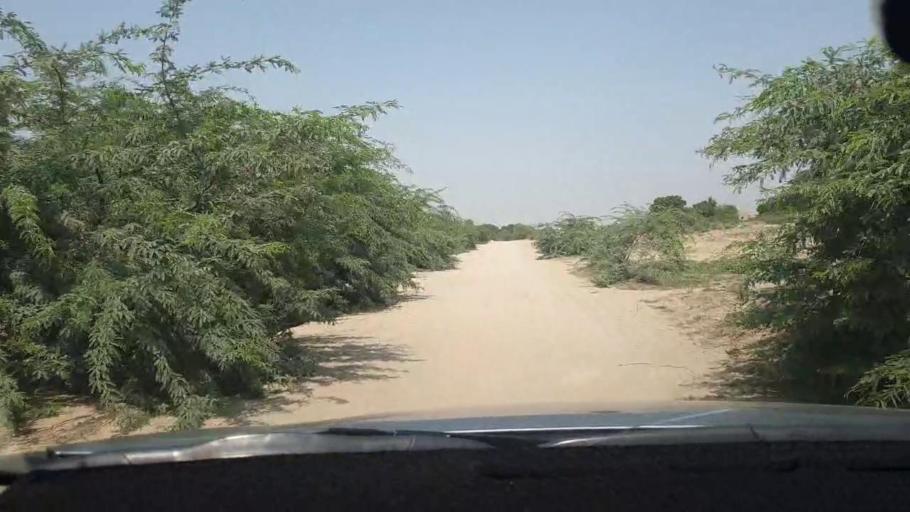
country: PK
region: Sindh
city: Tando Mittha Khan
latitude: 25.8478
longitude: 69.4242
